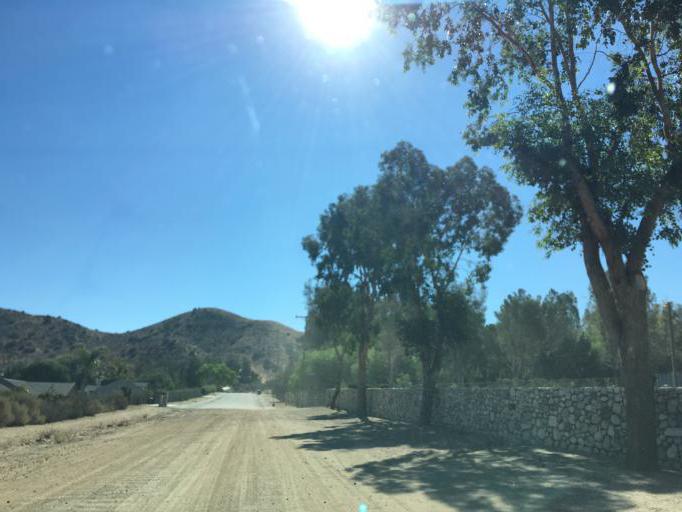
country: US
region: California
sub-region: Los Angeles County
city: Acton
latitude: 34.4628
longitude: -118.1701
